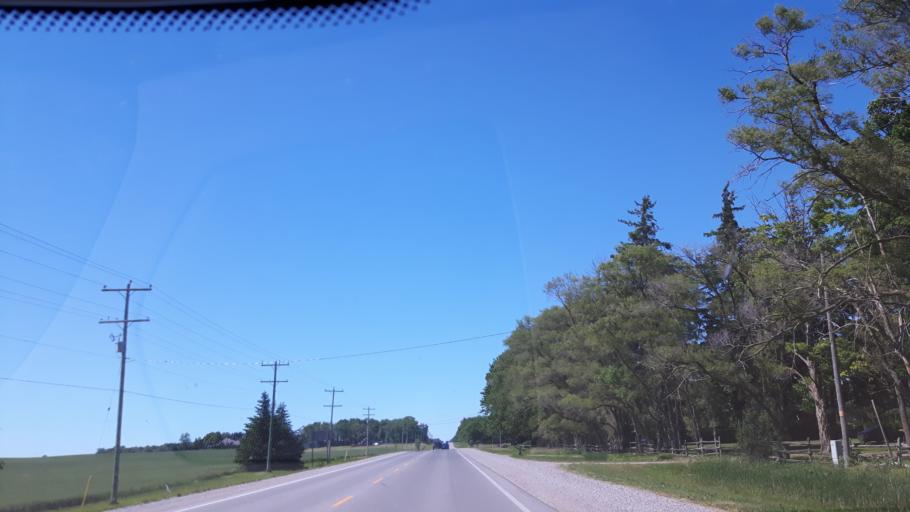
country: CA
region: Ontario
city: London
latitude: 43.0652
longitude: -81.3025
